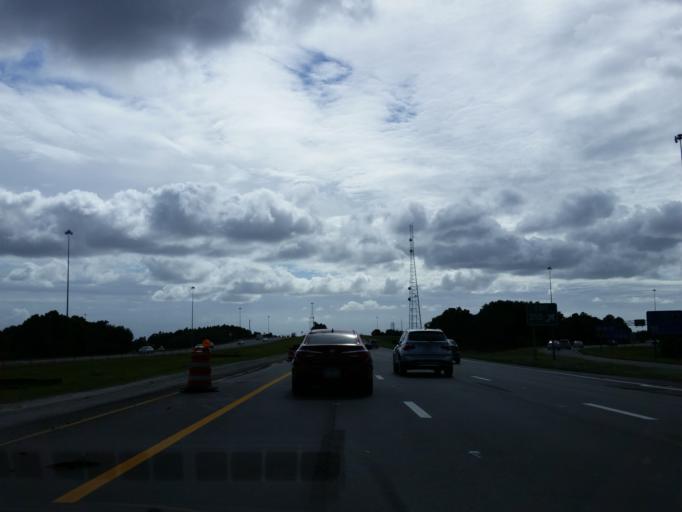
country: US
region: Florida
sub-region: Sarasota County
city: Fruitville
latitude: 27.3434
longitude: -82.4469
